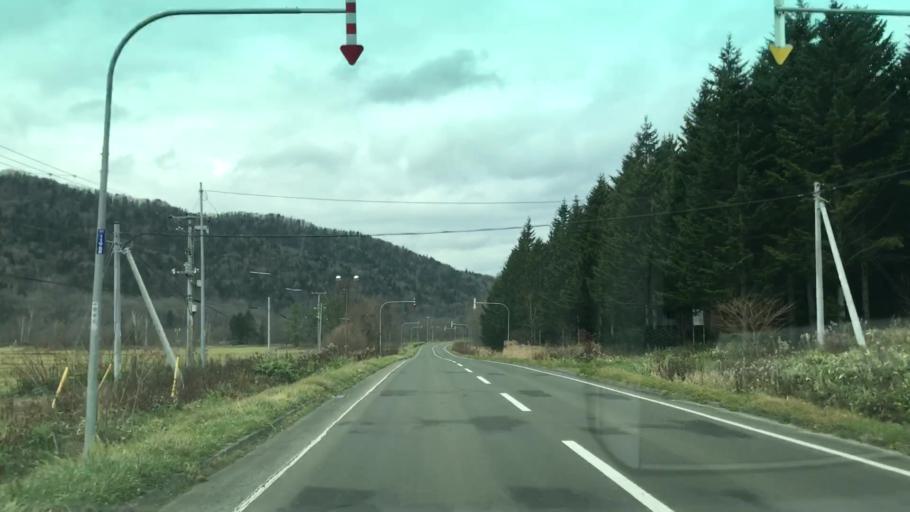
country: JP
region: Hokkaido
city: Shimo-furano
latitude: 42.9537
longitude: 142.4344
